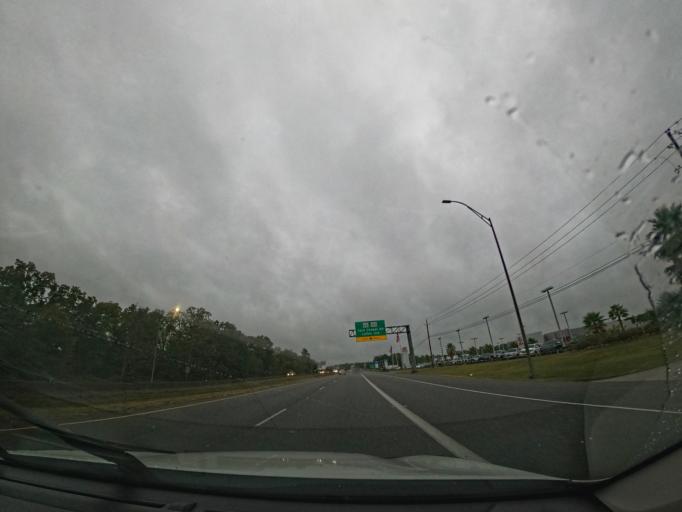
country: US
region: Texas
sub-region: Angelina County
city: Lufkin
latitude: 31.3226
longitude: -94.6964
